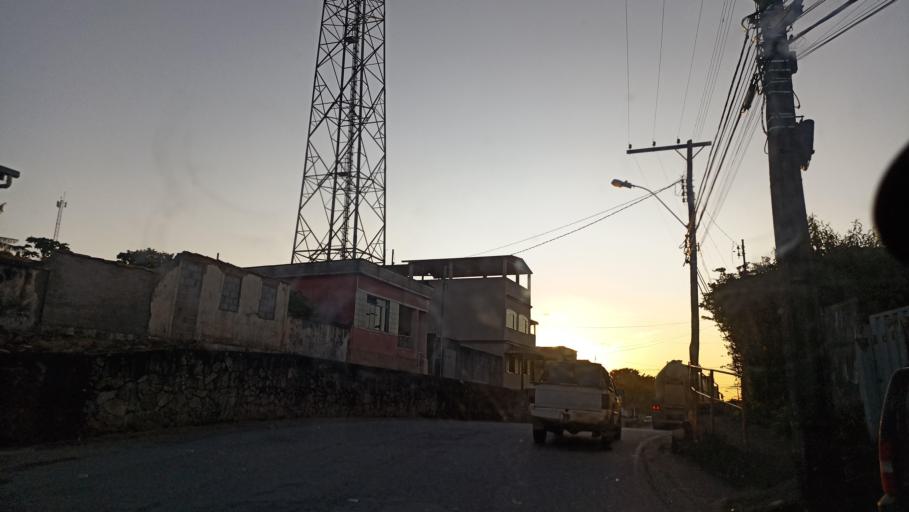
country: BR
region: Minas Gerais
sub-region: Sao Joao Del Rei
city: Sao Joao del Rei
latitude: -21.2438
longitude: -44.4142
